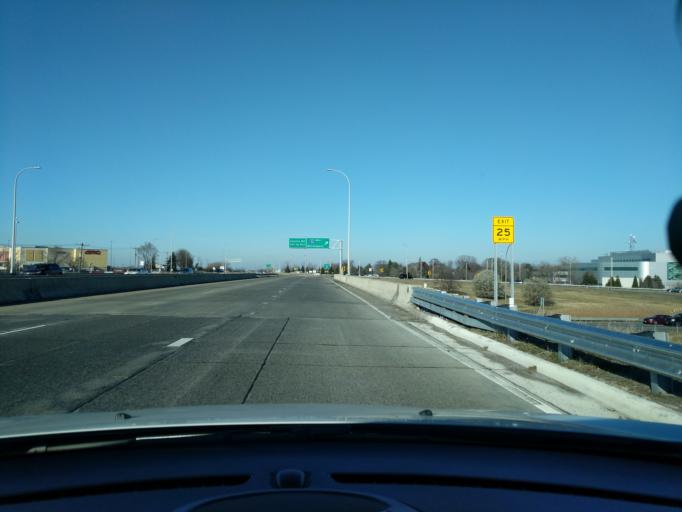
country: US
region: Minnesota
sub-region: Ramsey County
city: Roseville
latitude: 45.0098
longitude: -93.1664
